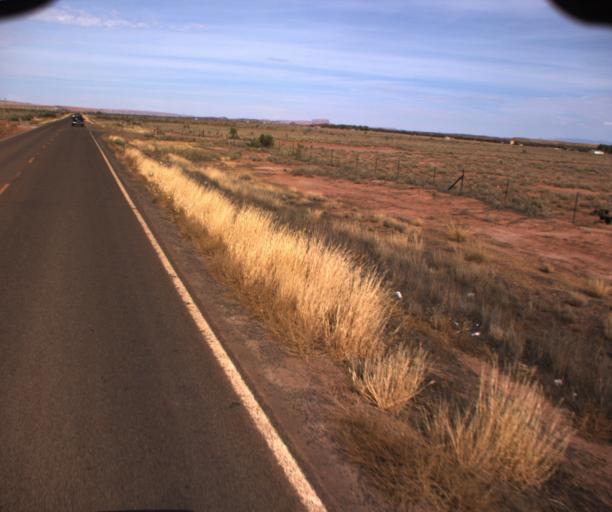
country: US
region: Arizona
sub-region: Apache County
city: Many Farms
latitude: 36.2827
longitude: -109.6027
